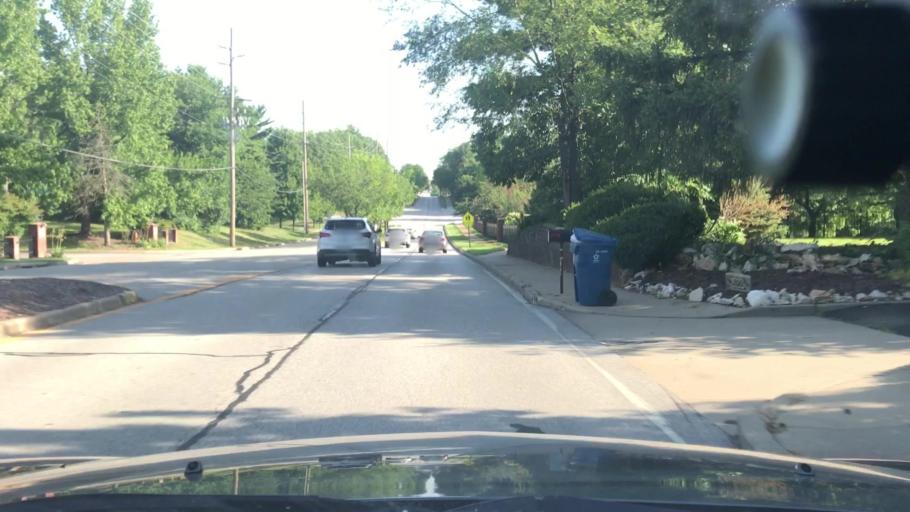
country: US
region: Missouri
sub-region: Saint Louis County
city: Creve Coeur
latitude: 38.6582
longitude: -90.4432
